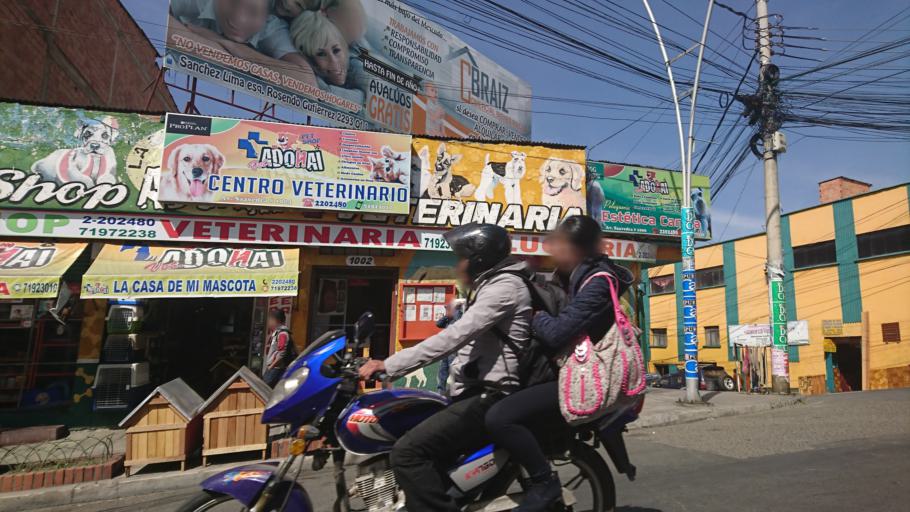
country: BO
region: La Paz
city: La Paz
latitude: -16.4973
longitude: -68.1279
